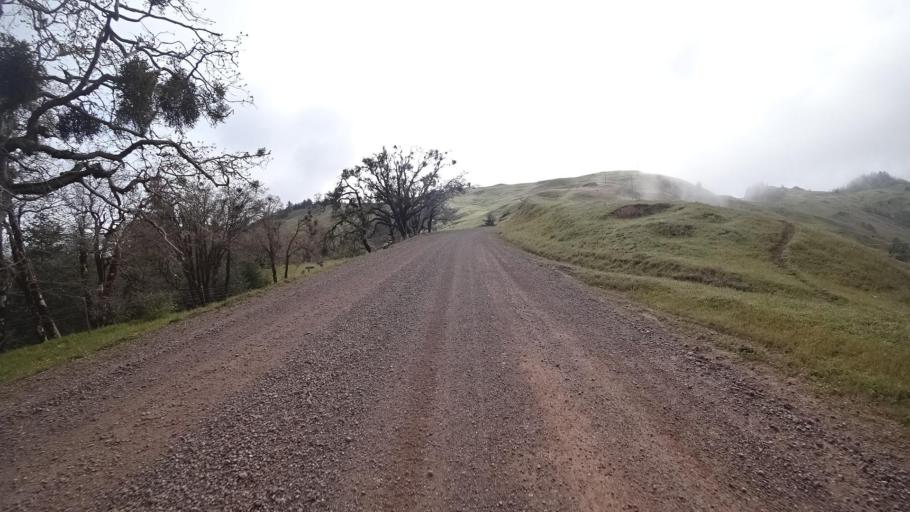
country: US
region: California
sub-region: Humboldt County
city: Redway
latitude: 40.2029
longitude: -123.7151
